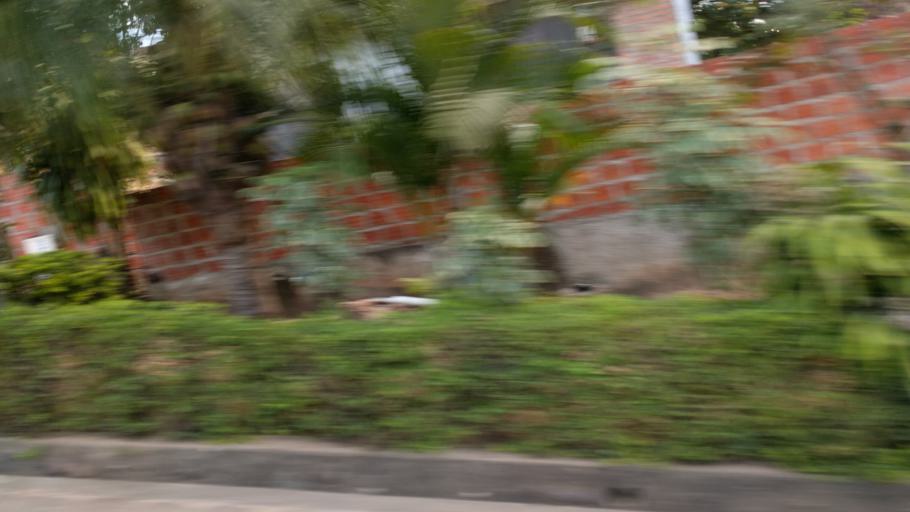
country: BO
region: Santa Cruz
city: Buena Vista
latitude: -17.4558
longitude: -63.6571
